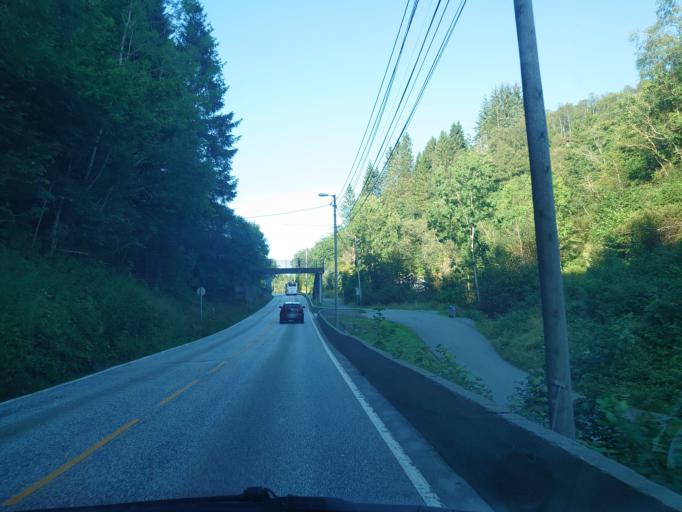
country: NO
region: Hordaland
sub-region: Bergen
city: Espeland
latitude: 60.3424
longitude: 5.4000
